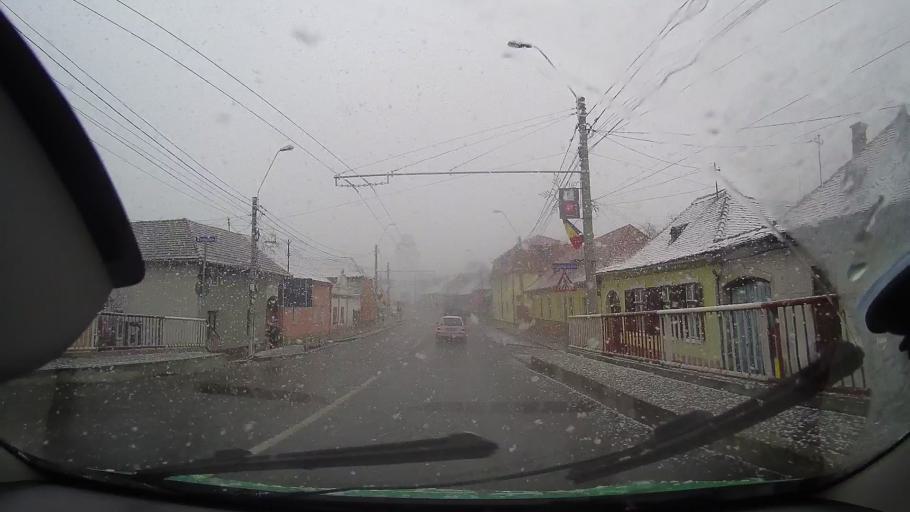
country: RO
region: Sibiu
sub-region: Municipiul Medias
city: Medias
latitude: 46.1698
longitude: 24.3480
